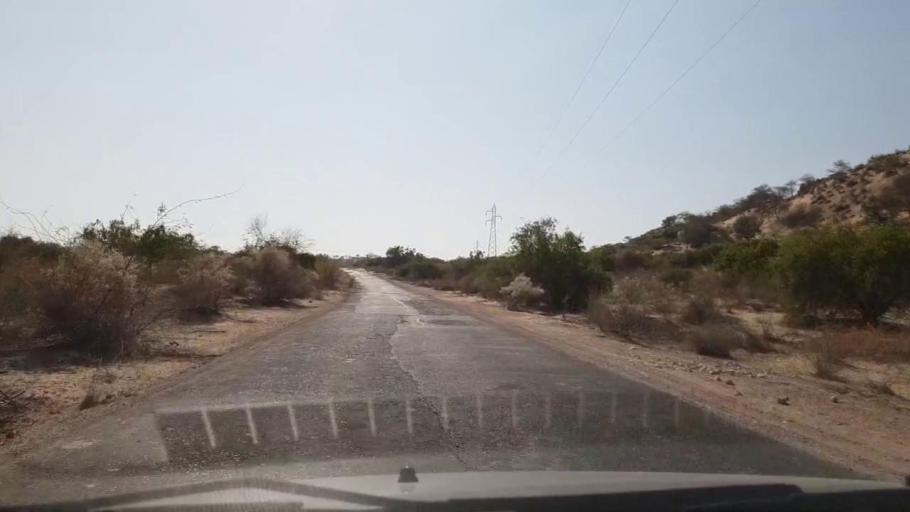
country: PK
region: Sindh
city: Mithi
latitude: 24.6395
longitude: 69.7437
